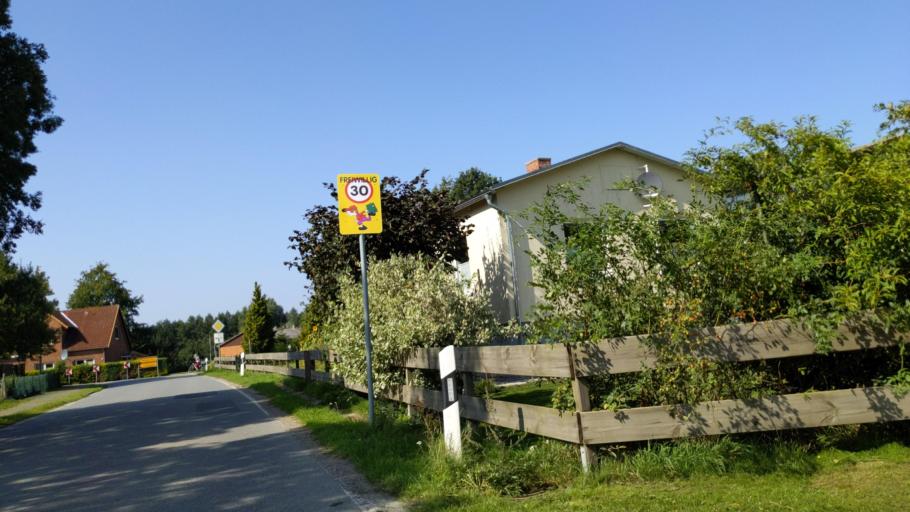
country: DE
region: Schleswig-Holstein
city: Gross Schenkenberg
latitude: 53.7966
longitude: 10.5624
